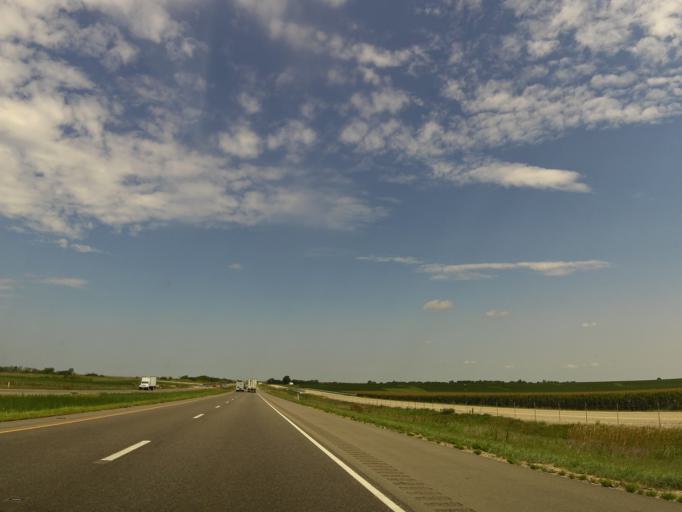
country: US
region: Illinois
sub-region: Marshall County
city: Wenona
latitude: 41.0804
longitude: -89.0674
